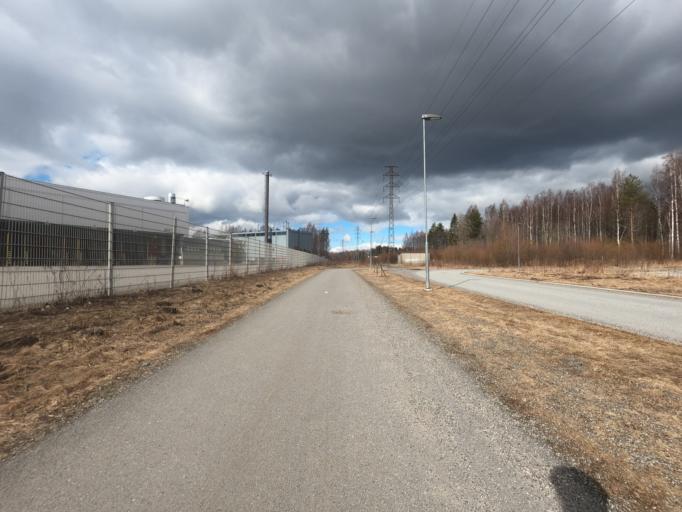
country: FI
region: North Karelia
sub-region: Joensuu
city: Joensuu
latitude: 62.6042
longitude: 29.7855
